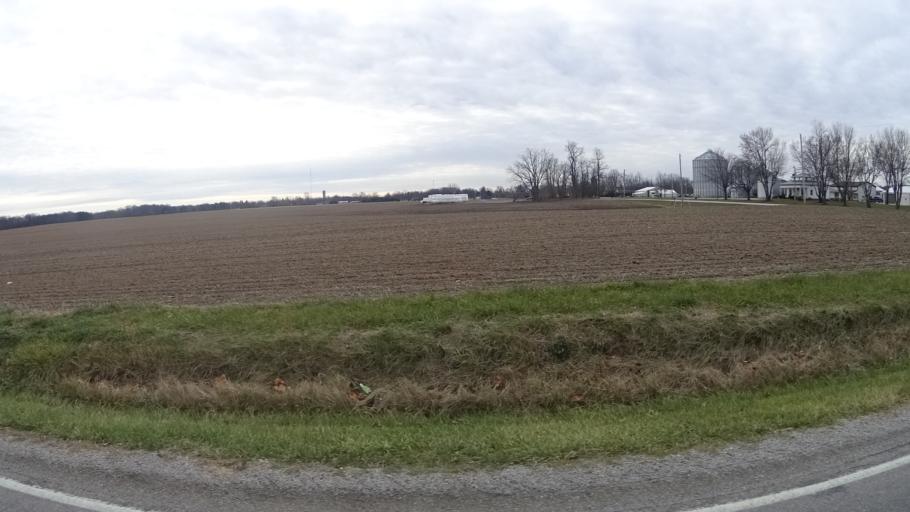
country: US
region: Ohio
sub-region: Lorain County
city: Wellington
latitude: 41.2000
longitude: -82.2158
